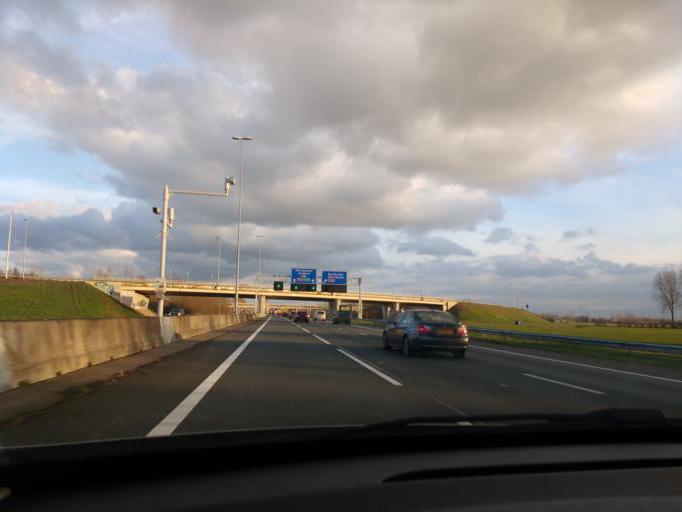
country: NL
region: Gelderland
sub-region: Gemeente Ede
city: Ederveen
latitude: 52.0272
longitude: 5.6086
